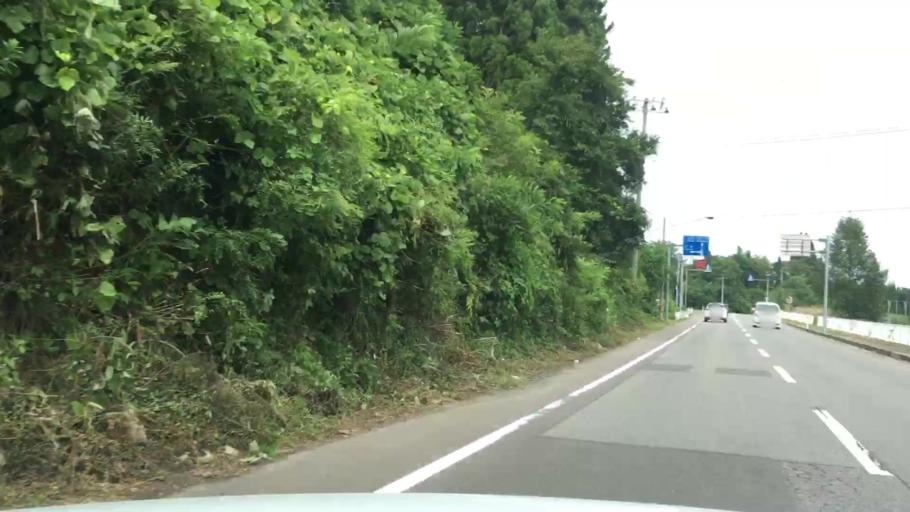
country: JP
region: Aomori
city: Shimokizukuri
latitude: 40.7495
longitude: 140.2294
